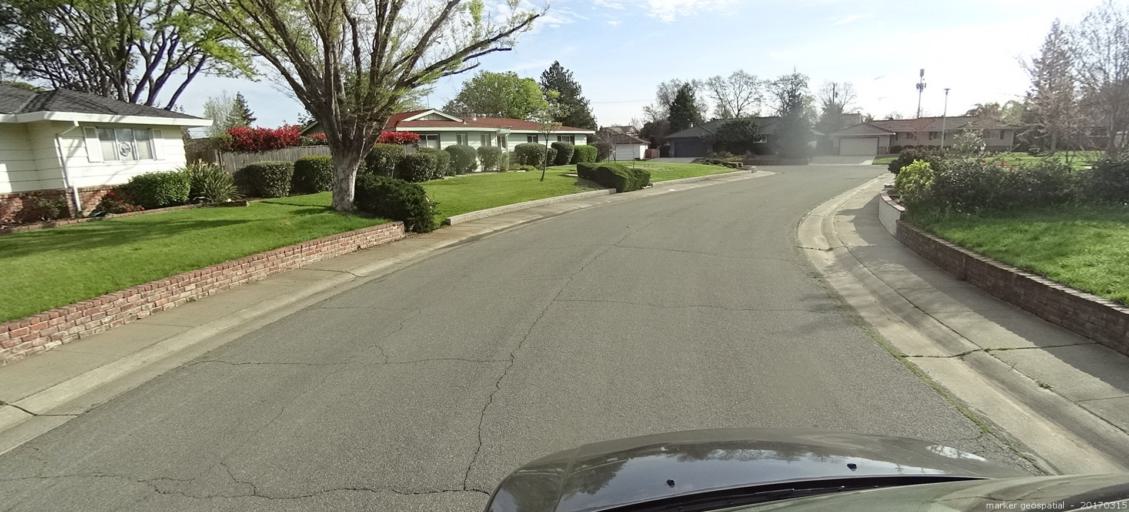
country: US
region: California
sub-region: Sacramento County
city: Parkway
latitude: 38.5079
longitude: -121.5077
